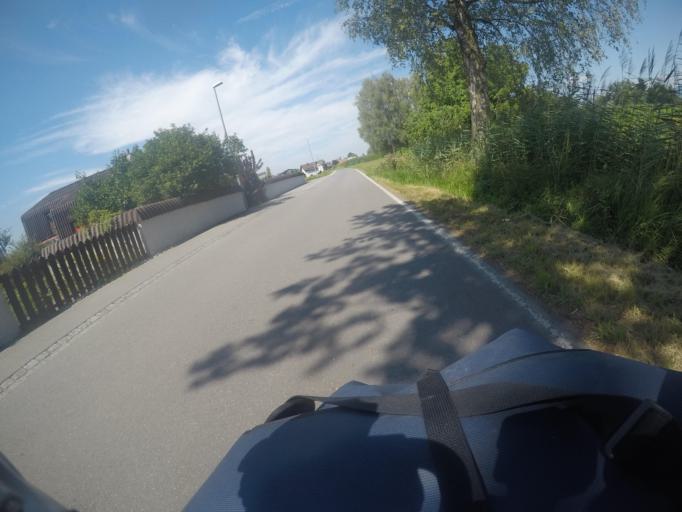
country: CH
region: Saint Gallen
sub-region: Wahlkreis Rheintal
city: Diepoldsau
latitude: 47.4057
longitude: 9.6606
